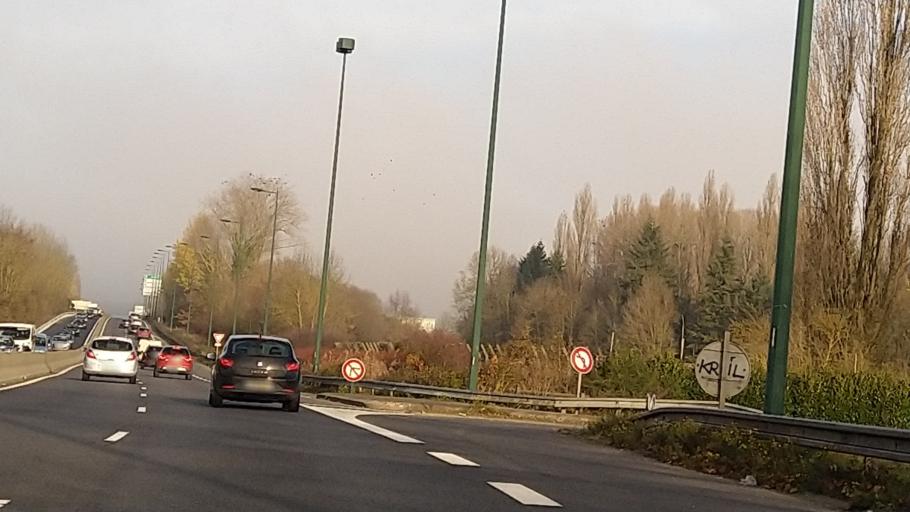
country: FR
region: Ile-de-France
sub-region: Departement du Val-d'Oise
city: Mours
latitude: 49.1345
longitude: 2.2562
